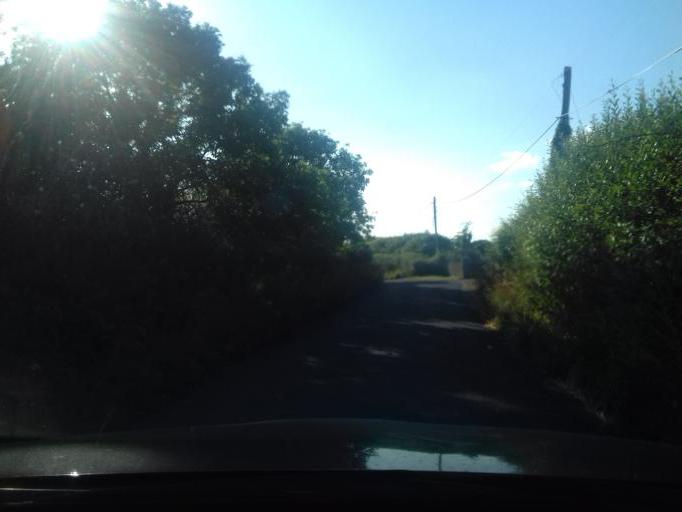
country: IE
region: Leinster
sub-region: An Mhi
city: Ashbourne
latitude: 53.4547
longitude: -6.3830
